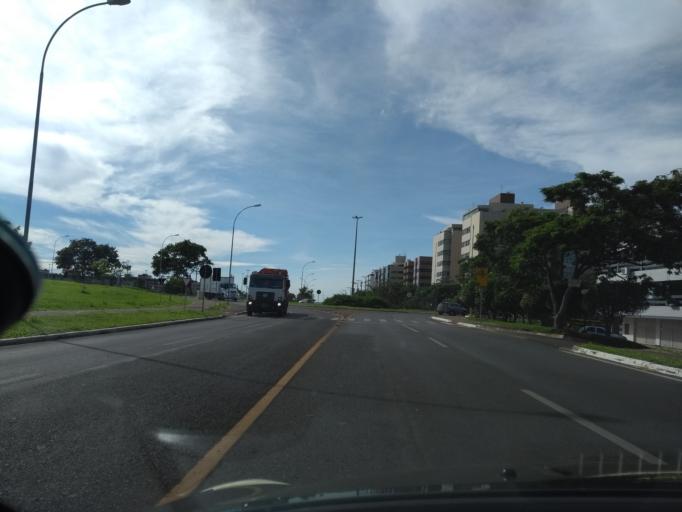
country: BR
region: Federal District
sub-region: Brasilia
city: Brasilia
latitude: -15.7942
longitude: -47.9280
